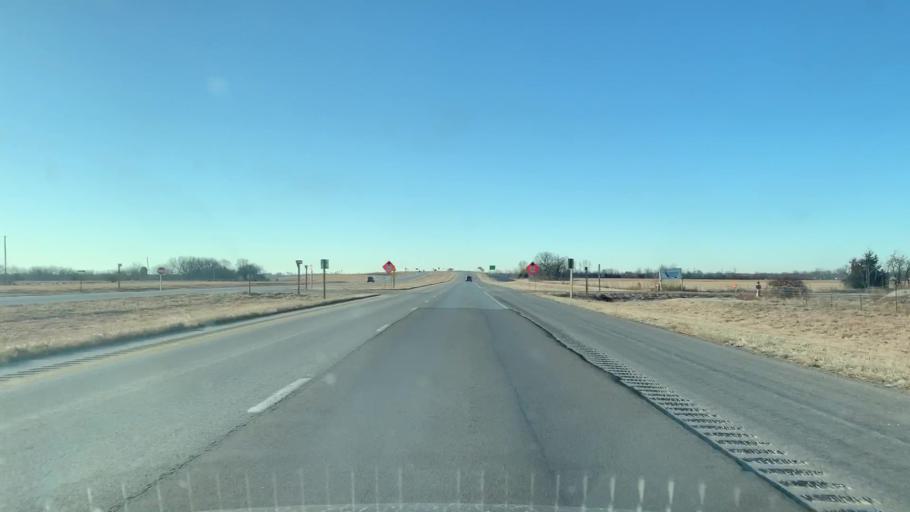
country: US
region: Kansas
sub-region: Bourbon County
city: Fort Scott
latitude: 37.7765
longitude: -94.7057
